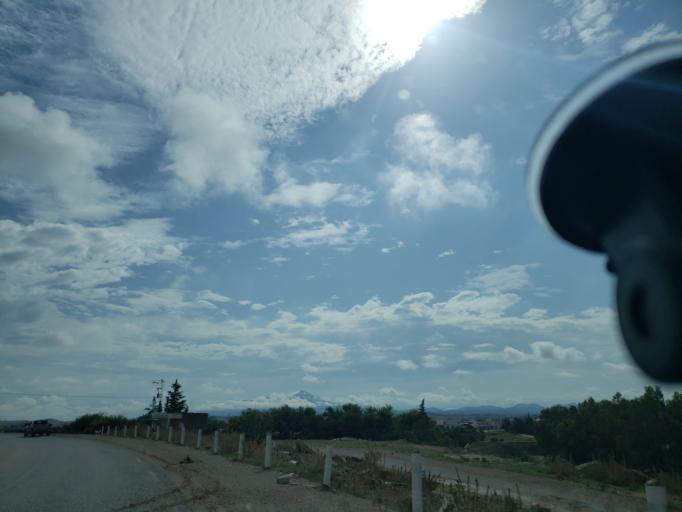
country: TN
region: Zaghwan
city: El Fahs
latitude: 36.3938
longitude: 9.9061
